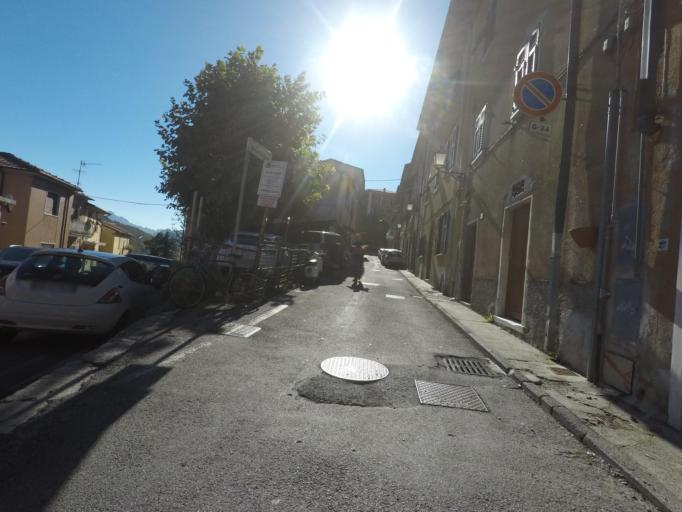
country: IT
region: Liguria
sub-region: Provincia di La Spezia
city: Casano-Dogana-Isola
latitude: 44.1127
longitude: 10.0741
